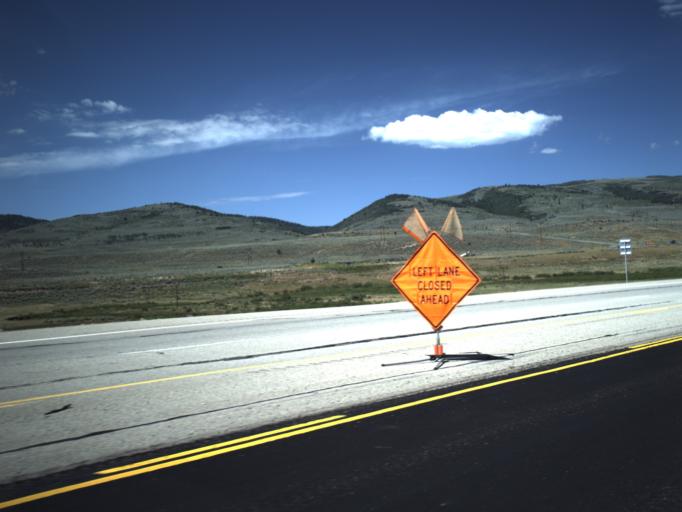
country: US
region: Utah
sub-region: Carbon County
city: Helper
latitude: 39.8583
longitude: -111.0227
